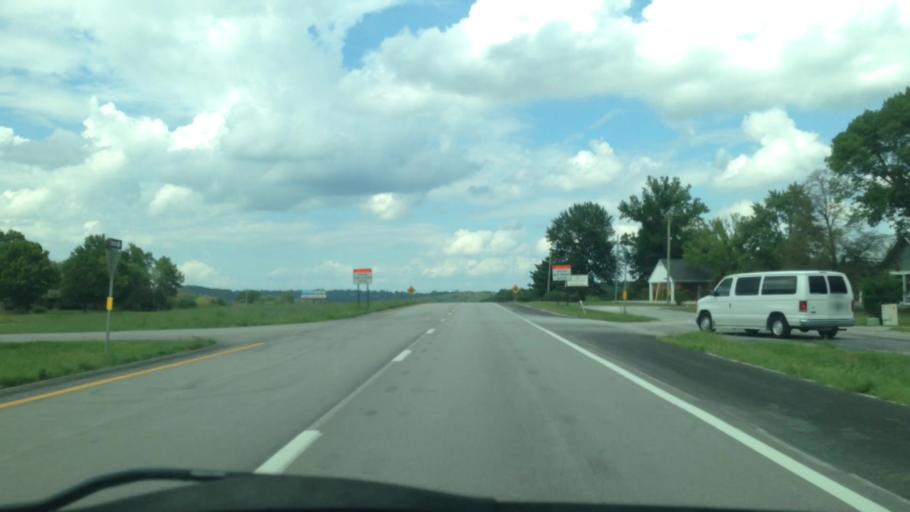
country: US
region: Missouri
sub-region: Marion County
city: Hannibal
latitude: 39.6651
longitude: -91.4168
